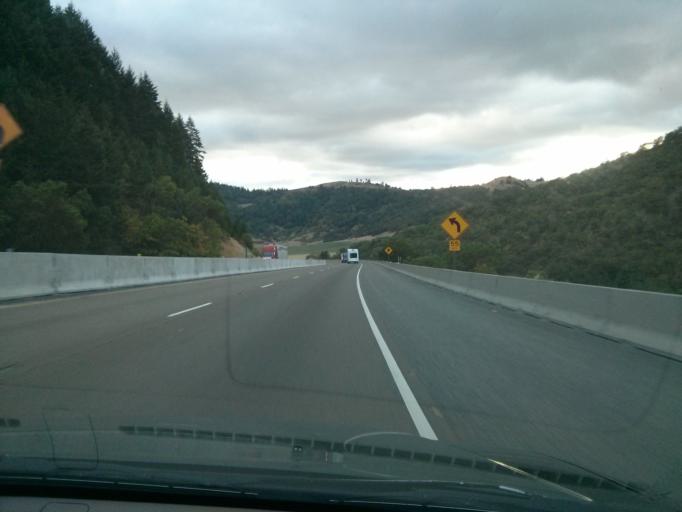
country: US
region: Oregon
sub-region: Douglas County
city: Winston
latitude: 43.1053
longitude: -123.3609
